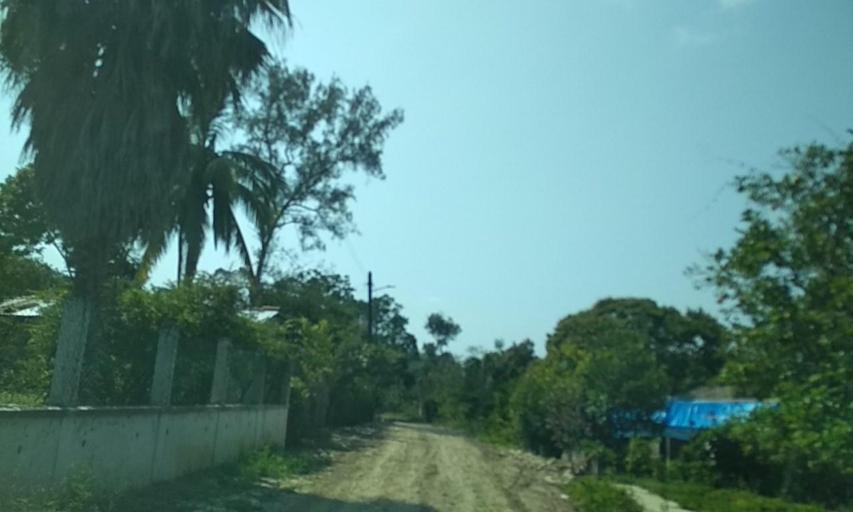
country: MX
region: Veracruz
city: Gutierrez Zamora
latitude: 20.3605
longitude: -97.1683
